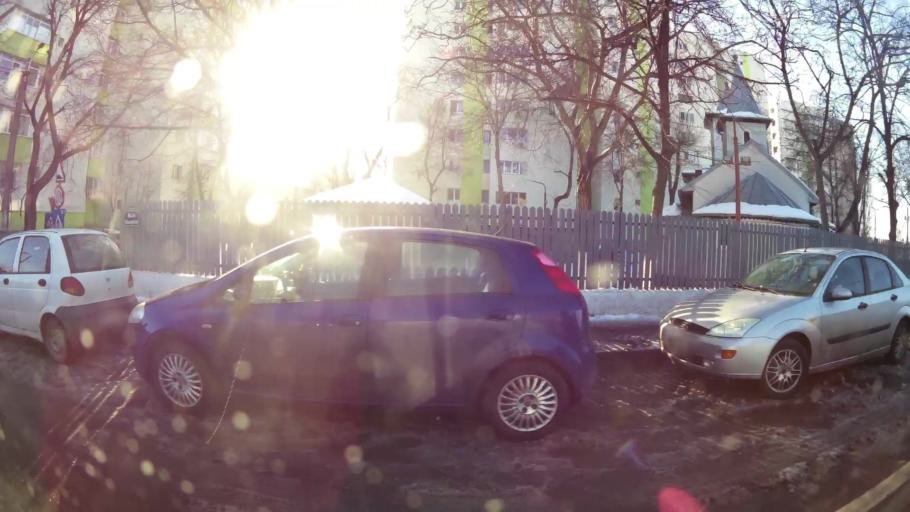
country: RO
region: Ilfov
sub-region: Comuna Fundeni-Dobroesti
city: Fundeni
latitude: 44.4697
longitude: 26.1420
